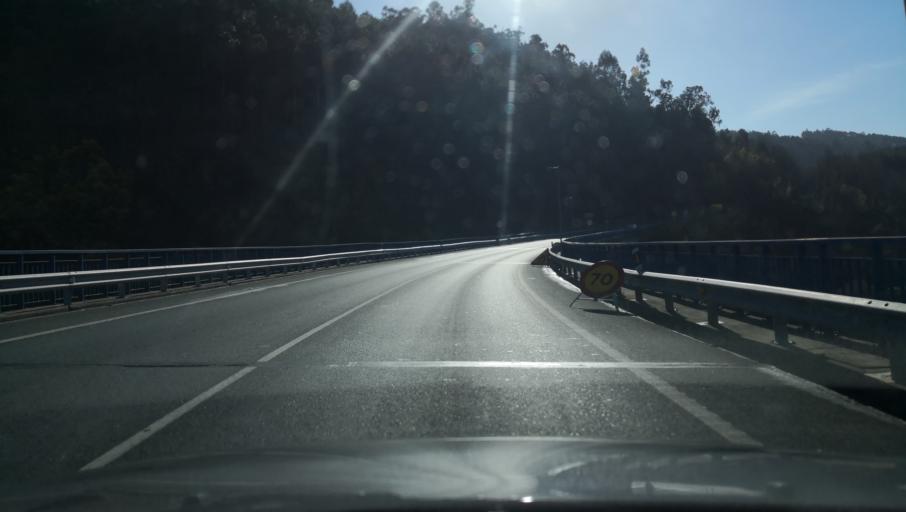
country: ES
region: Galicia
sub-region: Provincia da Coruna
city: Ribeira
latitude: 42.7769
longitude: -8.4022
